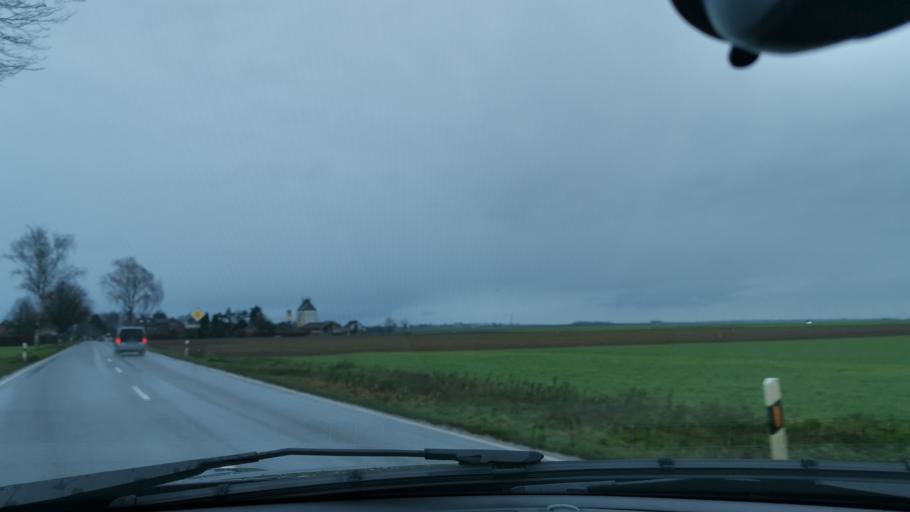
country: DE
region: North Rhine-Westphalia
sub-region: Regierungsbezirk Koln
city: Titz
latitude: 50.9812
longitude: 6.4386
